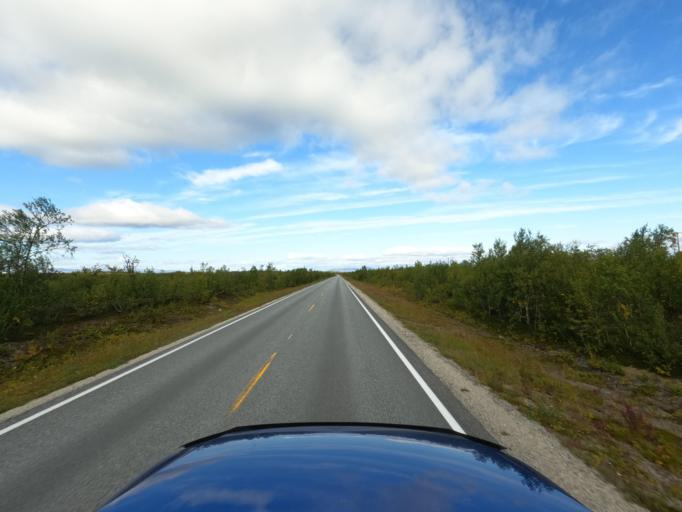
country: NO
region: Finnmark Fylke
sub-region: Karasjok
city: Karasjohka
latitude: 69.6572
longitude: 25.2776
